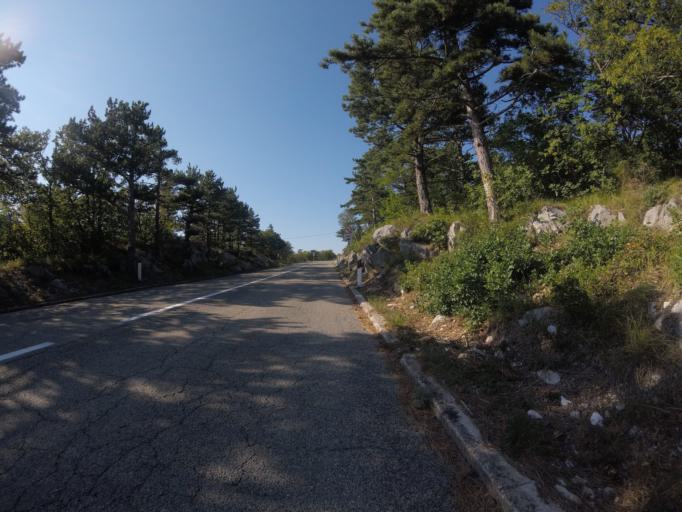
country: HR
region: Primorsko-Goranska
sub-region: Grad Crikvenica
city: Jadranovo
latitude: 45.2538
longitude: 14.6062
